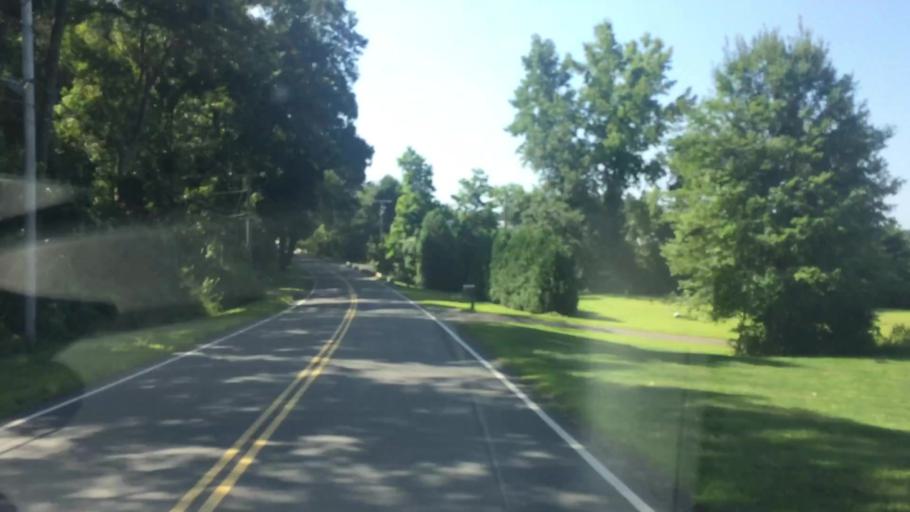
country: US
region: Massachusetts
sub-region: Hampshire County
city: Granby
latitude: 42.2551
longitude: -72.5421
